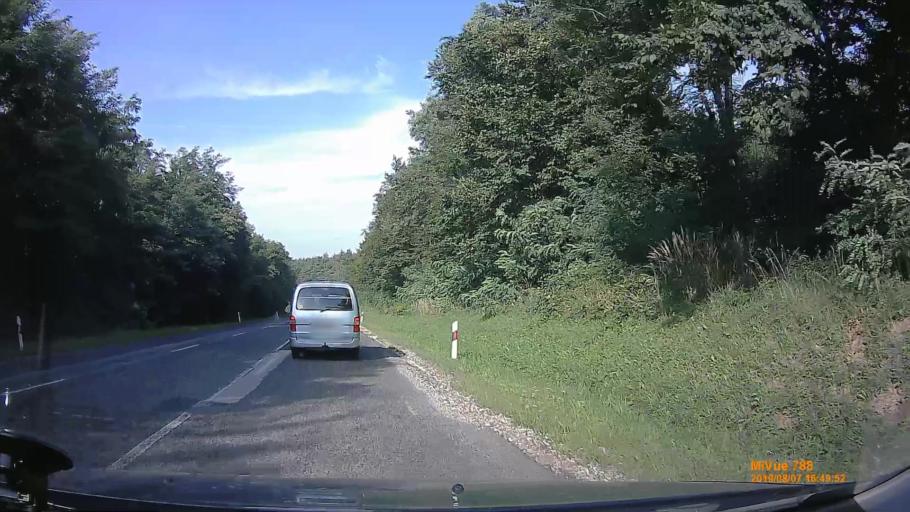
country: HU
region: Zala
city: Lenti
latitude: 46.6788
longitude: 16.6685
